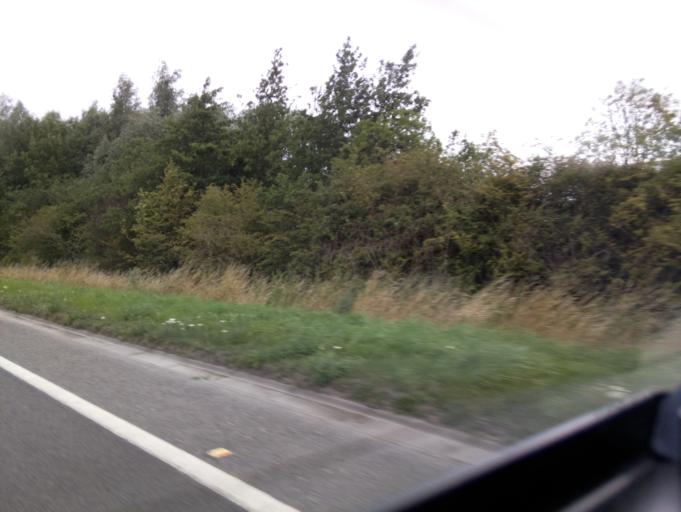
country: GB
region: England
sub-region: Wiltshire
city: Cricklade
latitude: 51.6473
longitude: -1.8517
